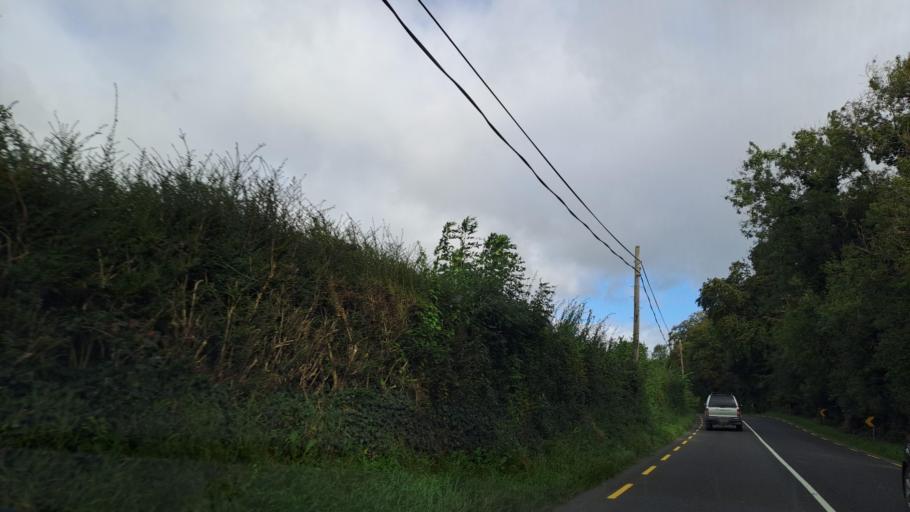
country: IE
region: Ulster
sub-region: County Monaghan
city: Carrickmacross
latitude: 53.9580
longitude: -6.7522
